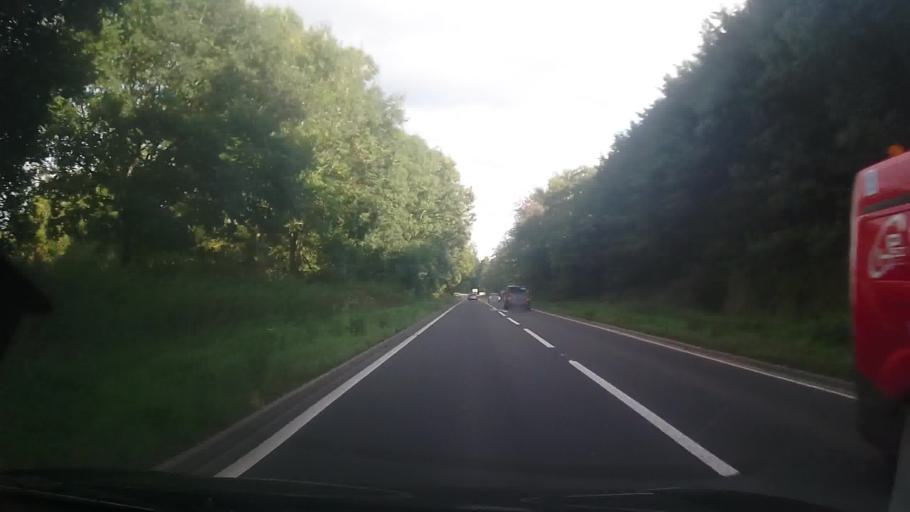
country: GB
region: England
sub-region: Shropshire
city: Bromfield
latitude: 52.3896
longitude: -2.7677
